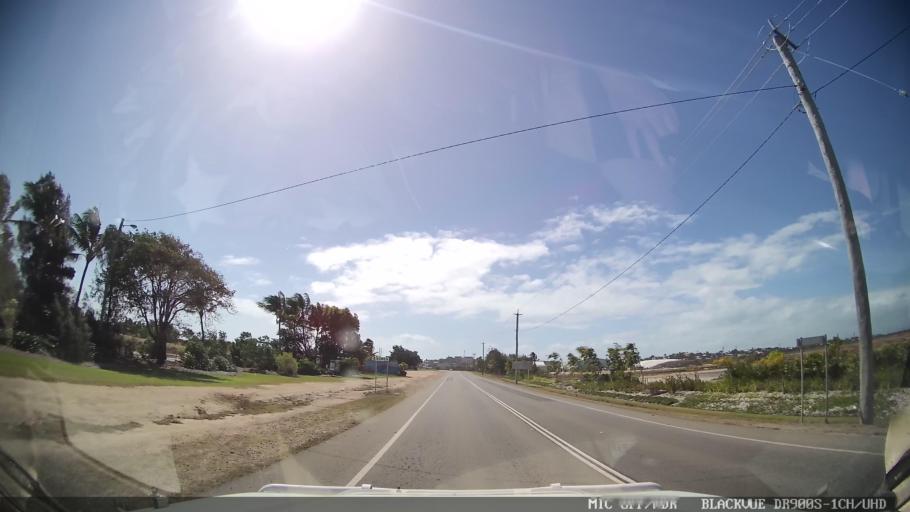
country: AU
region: Queensland
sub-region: Whitsunday
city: Bowen
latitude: -20.0141
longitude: 148.2230
